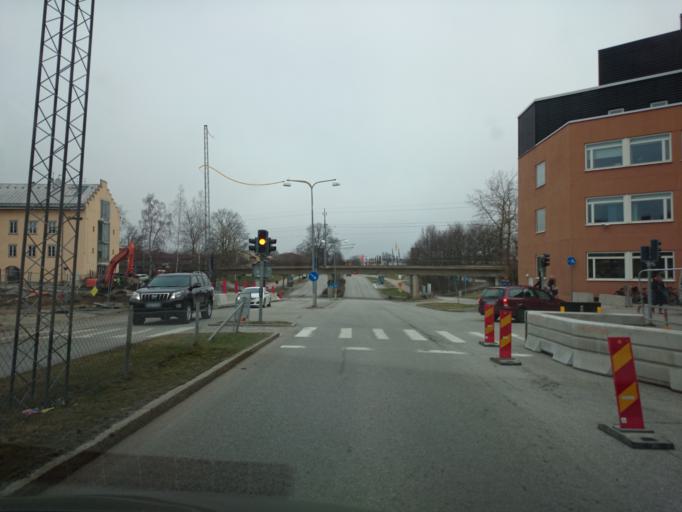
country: SE
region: Uppsala
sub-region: Uppsala Kommun
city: Uppsala
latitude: 59.8655
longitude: 17.6303
